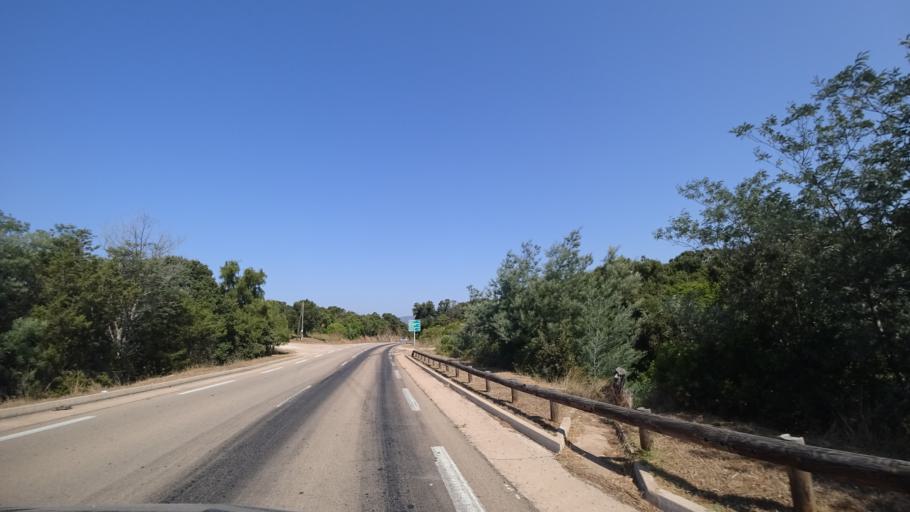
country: FR
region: Corsica
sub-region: Departement de la Corse-du-Sud
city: Bonifacio
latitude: 41.4723
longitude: 9.0928
